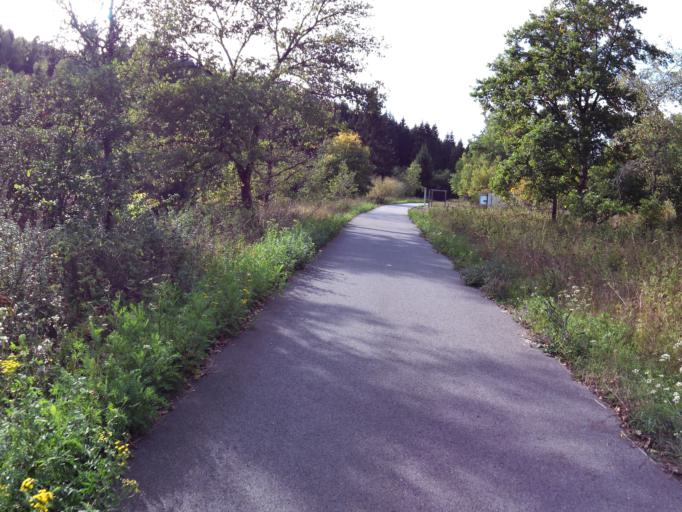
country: DE
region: Rheinland-Pfalz
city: Winterspelt
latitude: 50.2329
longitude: 6.1615
